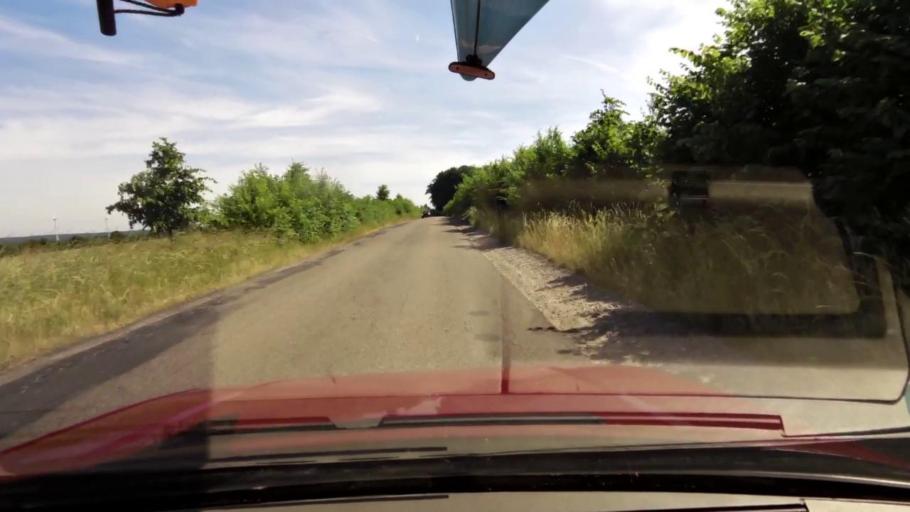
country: PL
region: Pomeranian Voivodeship
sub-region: Powiat slupski
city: Kobylnica
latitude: 54.3722
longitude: 16.9665
